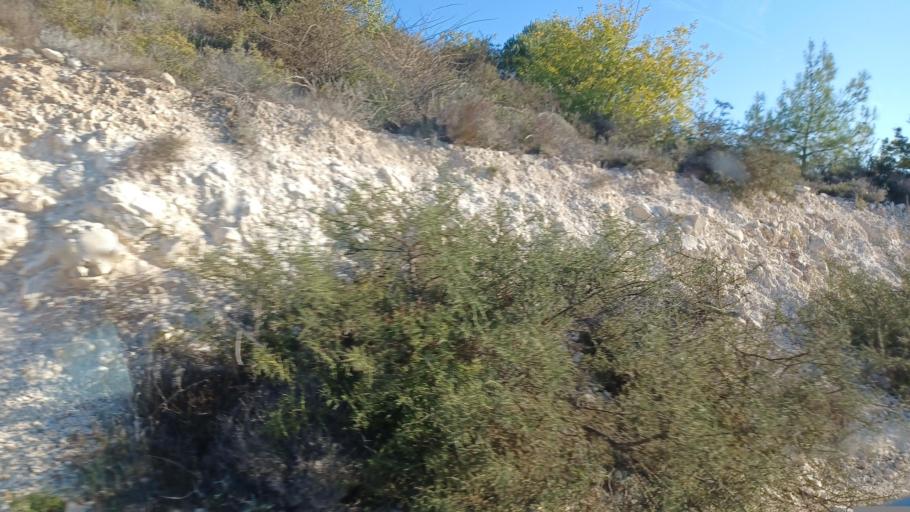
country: CY
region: Pafos
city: Polis
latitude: 34.9808
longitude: 32.5149
